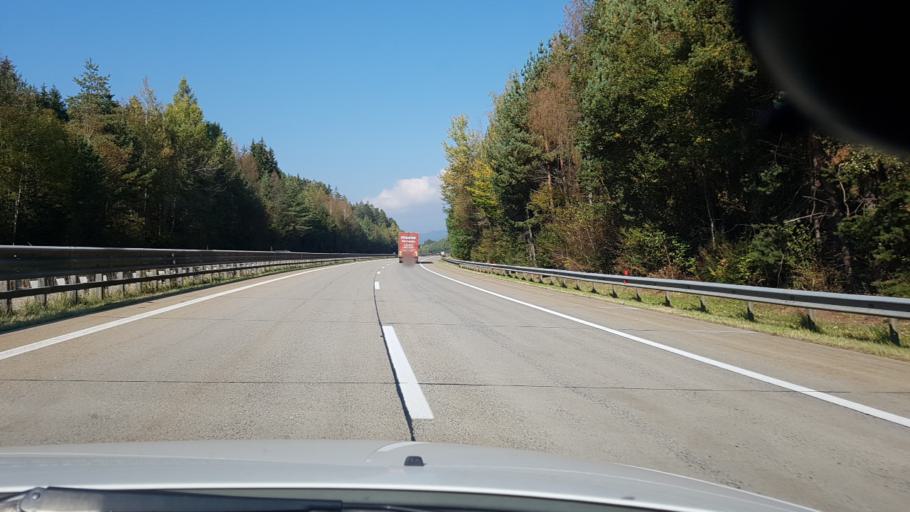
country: AT
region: Carinthia
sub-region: Politischer Bezirk Villach Land
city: Paternion
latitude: 46.7149
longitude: 13.6219
